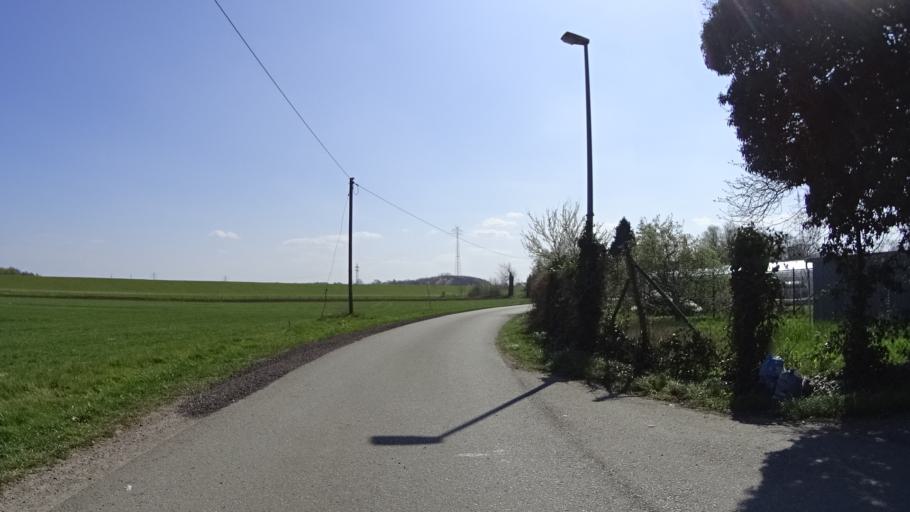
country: DE
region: Lower Saxony
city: Papenburg
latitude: 53.1099
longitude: 7.3615
